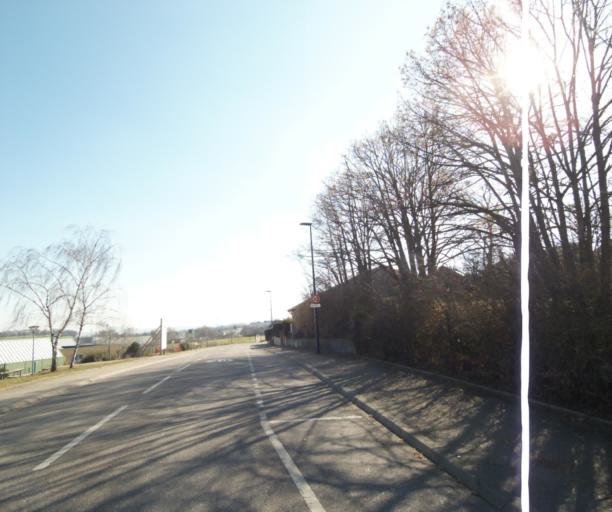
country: FR
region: Lorraine
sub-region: Departement de Meurthe-et-Moselle
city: Vandoeuvre-les-Nancy
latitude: 48.6435
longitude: 6.1769
